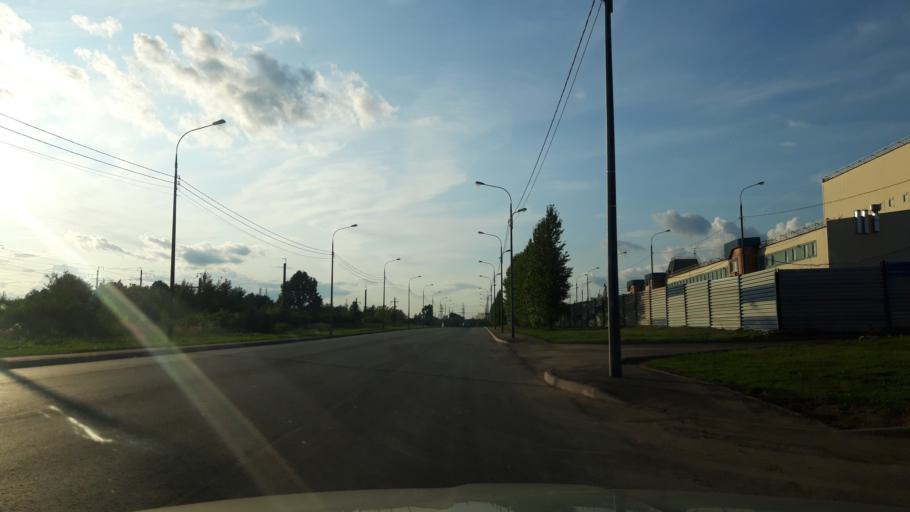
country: RU
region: Moskovskaya
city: Alabushevo
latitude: 56.0053
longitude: 37.1457
